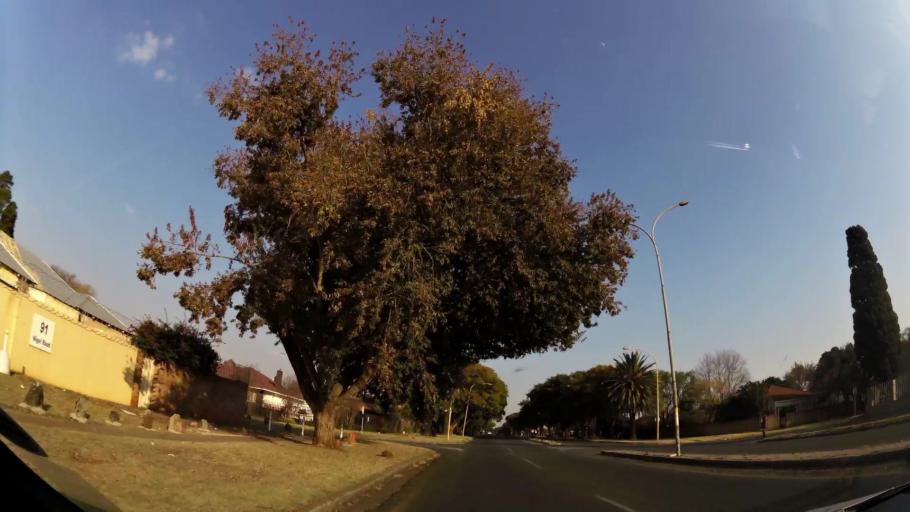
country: ZA
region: Gauteng
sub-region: Ekurhuleni Metropolitan Municipality
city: Springs
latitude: -26.2861
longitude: 28.4448
